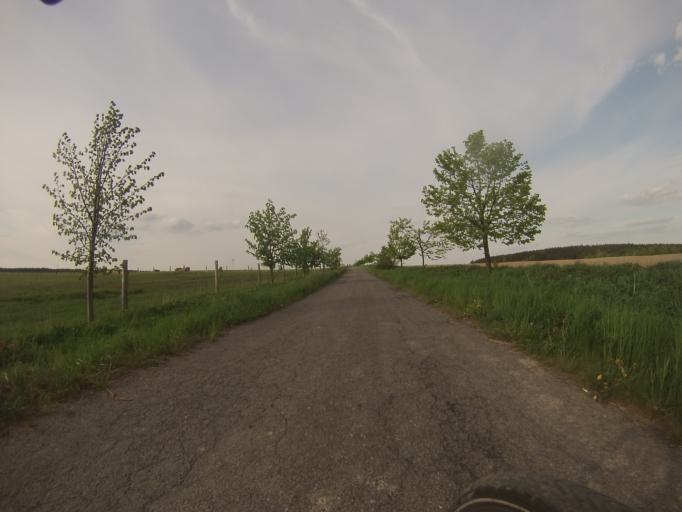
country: CZ
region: Olomoucky
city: Protivanov
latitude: 49.4468
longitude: 16.8616
